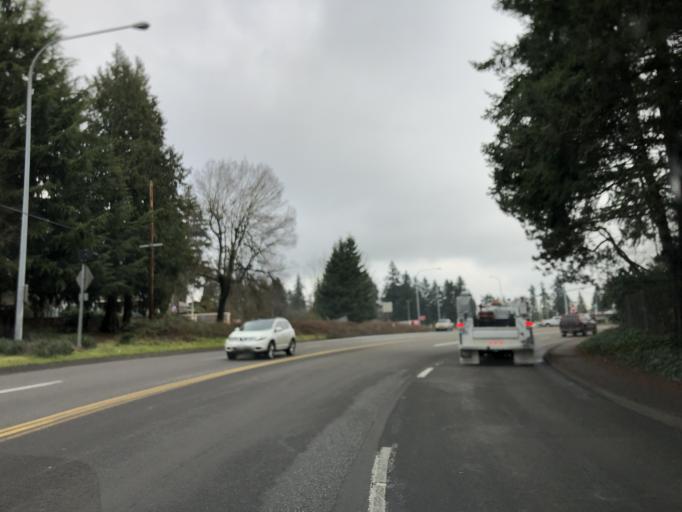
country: US
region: Washington
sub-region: Clark County
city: Vancouver
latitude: 45.6401
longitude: -122.6655
